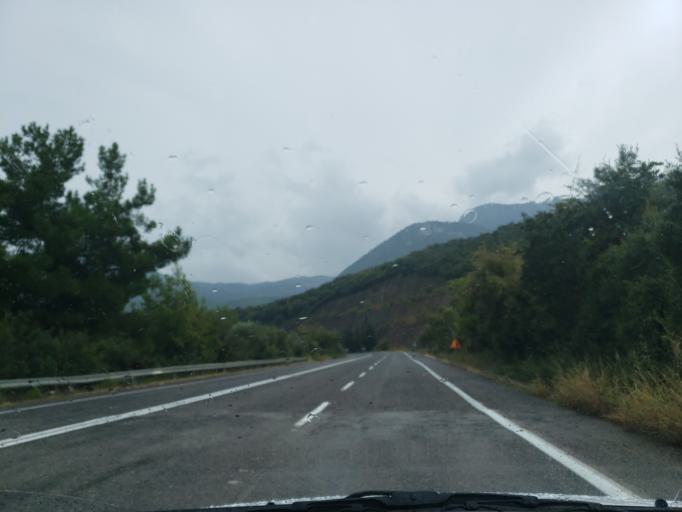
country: GR
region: Central Greece
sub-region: Nomos Fthiotidos
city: Anthili
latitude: 38.7897
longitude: 22.4807
